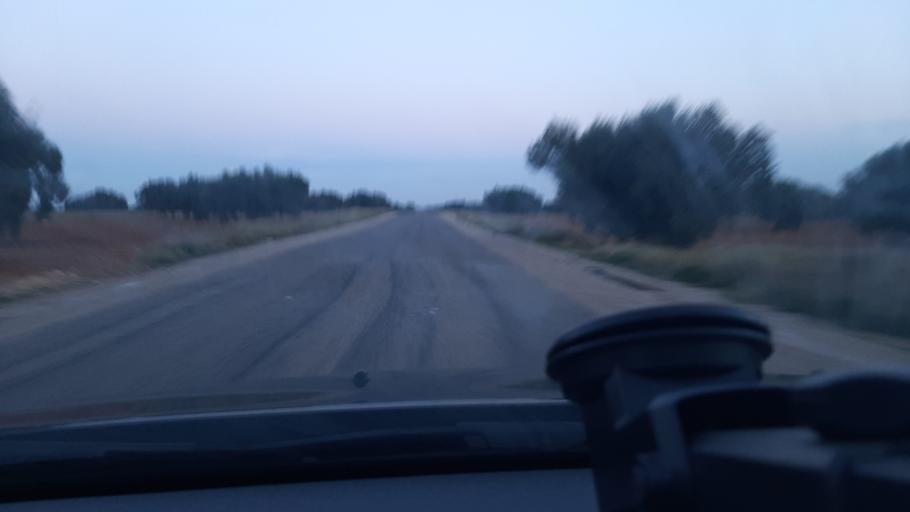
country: TN
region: Al Mahdiyah
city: Shurban
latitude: 35.0295
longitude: 10.4820
